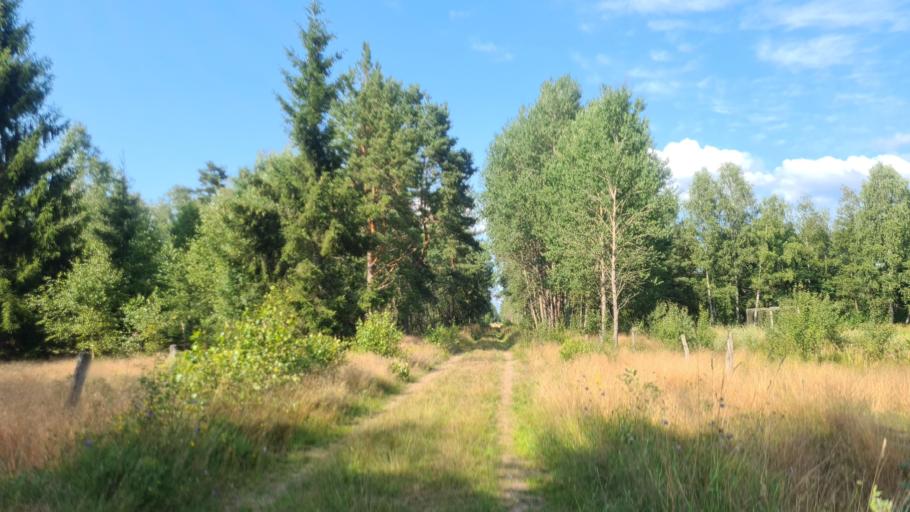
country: SE
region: Kronoberg
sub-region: Ljungby Kommun
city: Ljungby
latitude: 56.7626
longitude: 13.8916
